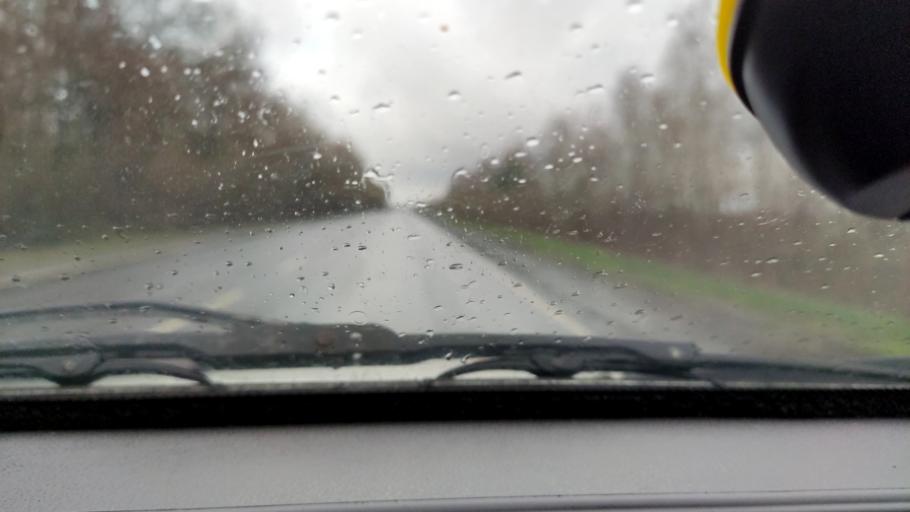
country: RU
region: Samara
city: Povolzhskiy
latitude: 53.6067
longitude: 49.6082
